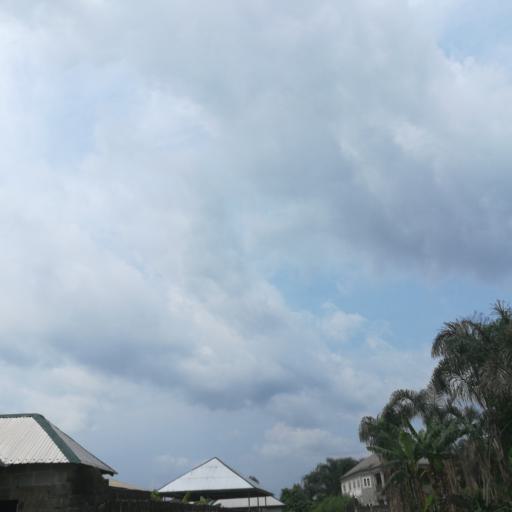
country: NG
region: Rivers
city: Port Harcourt
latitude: 4.8718
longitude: 7.0236
